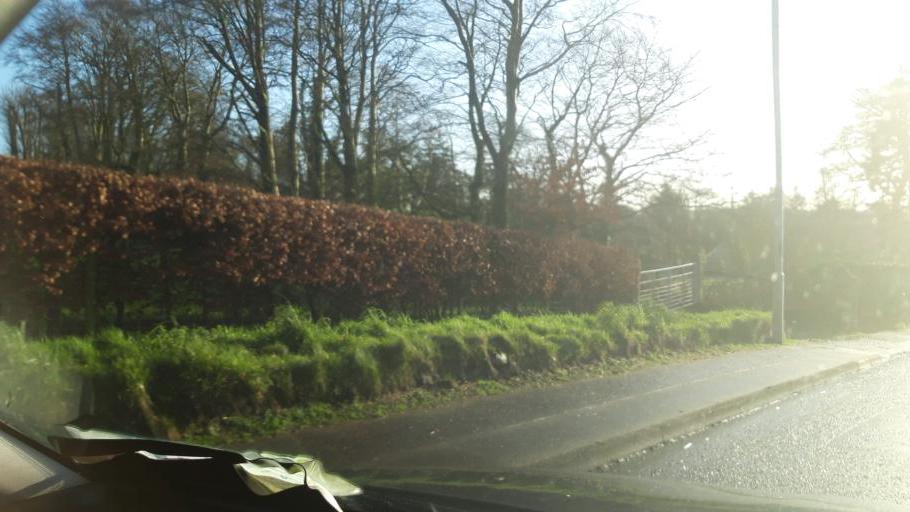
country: GB
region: Northern Ireland
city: Garvagh
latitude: 54.9881
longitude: -6.6855
